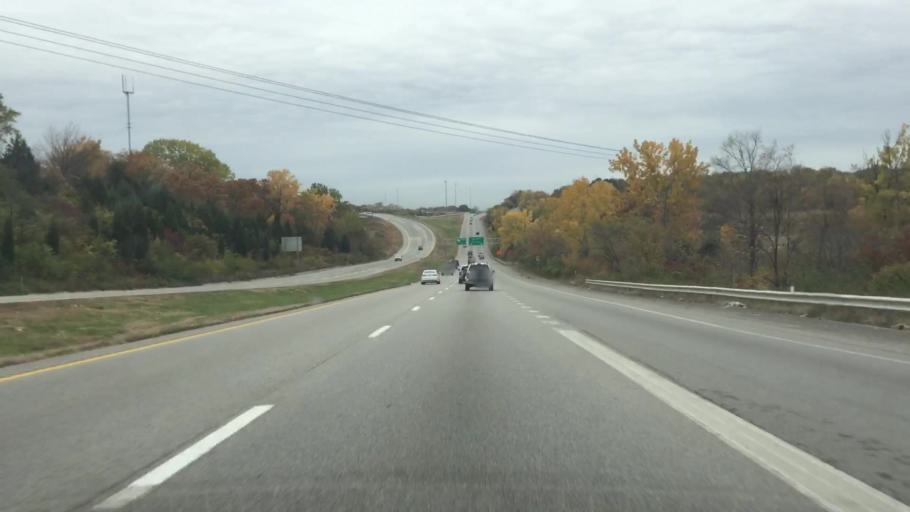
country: US
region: Missouri
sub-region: Jackson County
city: Raytown
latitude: 39.0113
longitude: -94.4907
